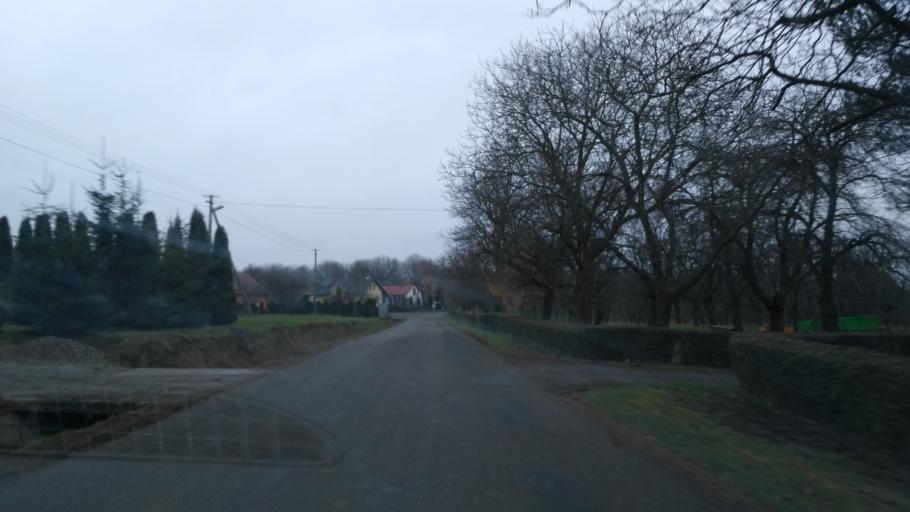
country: PL
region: Subcarpathian Voivodeship
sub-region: Powiat jaroslawski
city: Pruchnik
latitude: 49.9140
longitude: 22.5326
